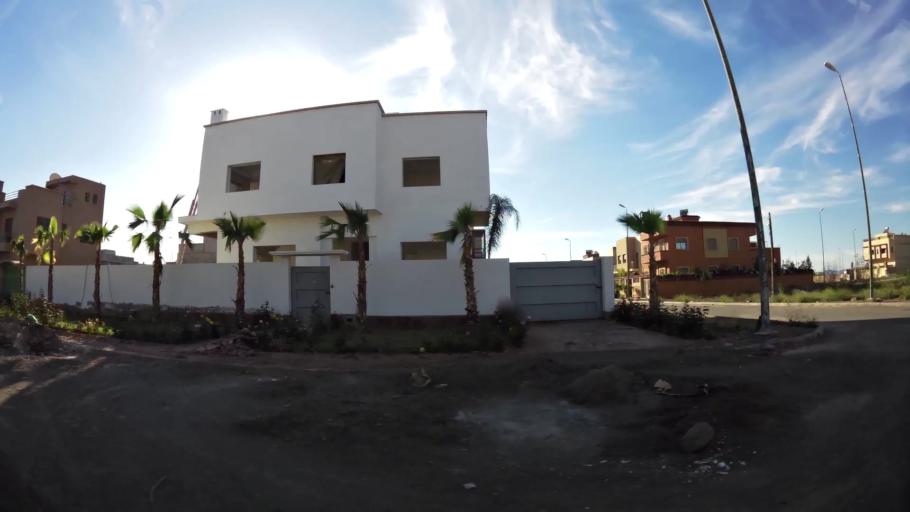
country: MA
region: Marrakech-Tensift-Al Haouz
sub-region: Marrakech
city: Marrakesh
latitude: 31.6710
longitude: -8.0712
